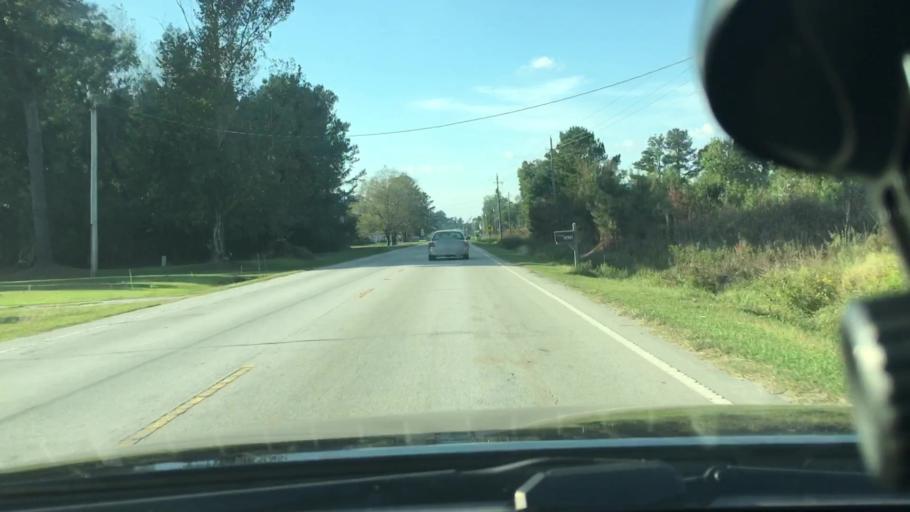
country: US
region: North Carolina
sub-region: Pitt County
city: Windsor
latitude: 35.4598
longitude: -77.2708
